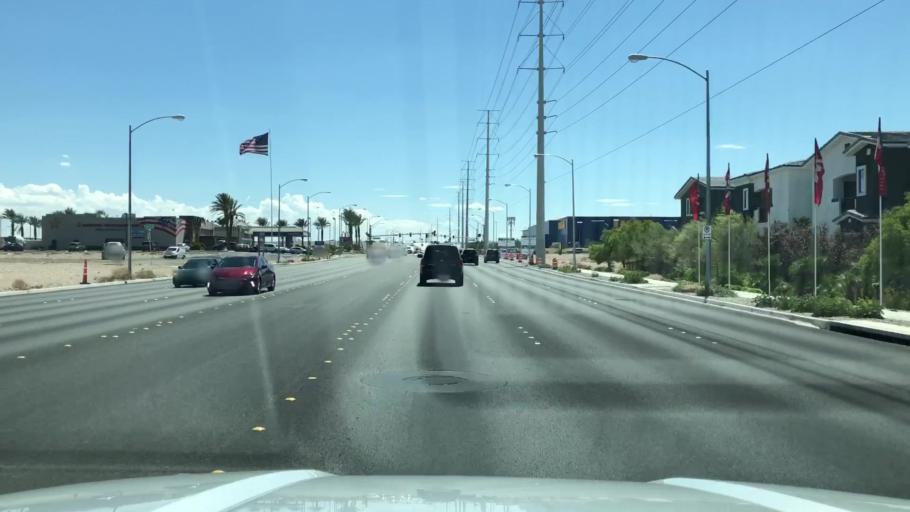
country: US
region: Nevada
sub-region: Clark County
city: Spring Valley
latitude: 36.0729
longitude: -115.2795
